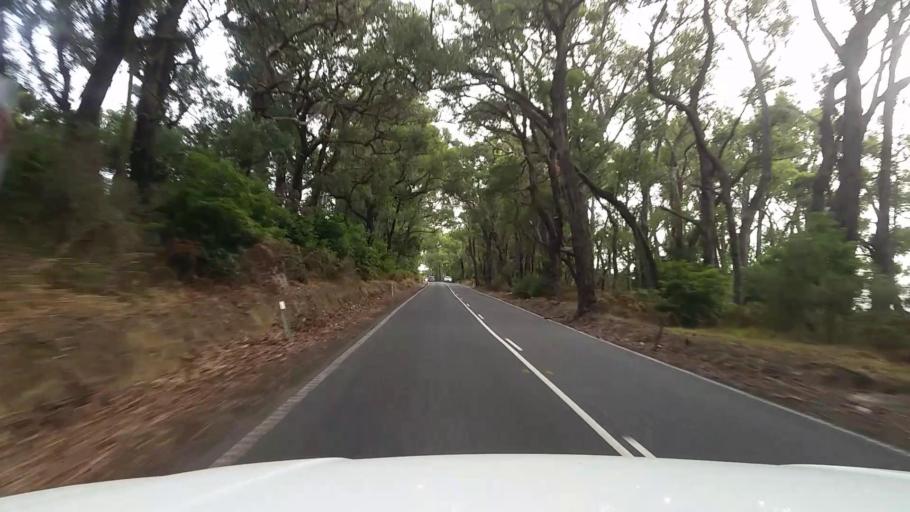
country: AU
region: Victoria
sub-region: Mornington Peninsula
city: Balnarring
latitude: -38.3351
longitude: 145.0958
